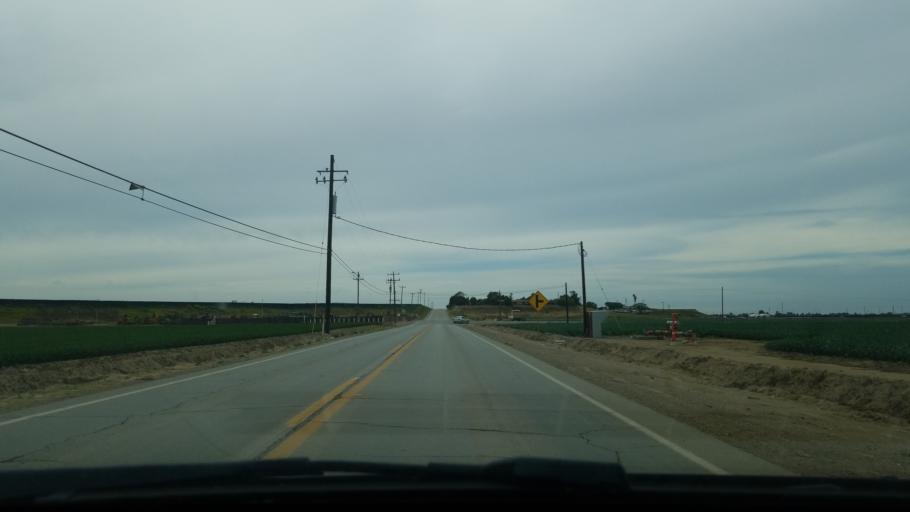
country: US
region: California
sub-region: Santa Barbara County
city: Santa Maria
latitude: 34.9234
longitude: -120.3723
